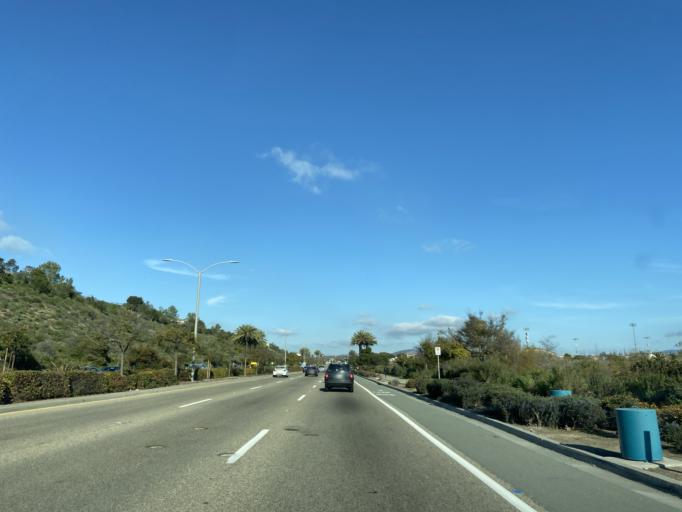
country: US
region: California
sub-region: San Diego County
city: Bonita
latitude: 32.6185
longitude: -116.9973
